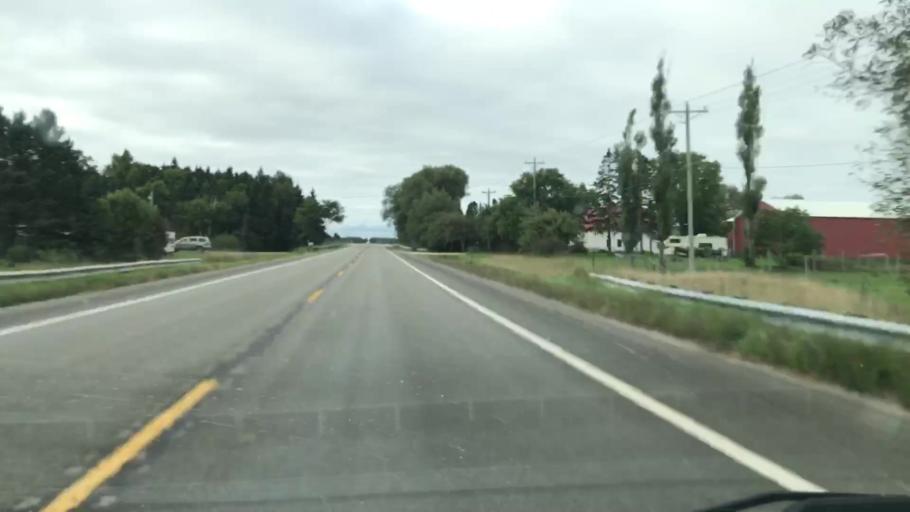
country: US
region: Michigan
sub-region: Luce County
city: Newberry
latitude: 46.1568
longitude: -85.5713
